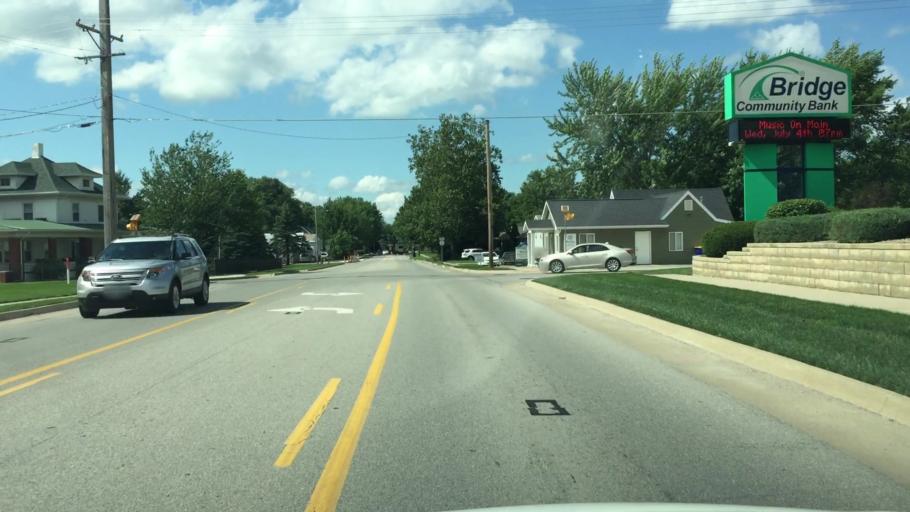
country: US
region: Iowa
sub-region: Johnson County
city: Solon
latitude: 41.8018
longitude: -91.4915
